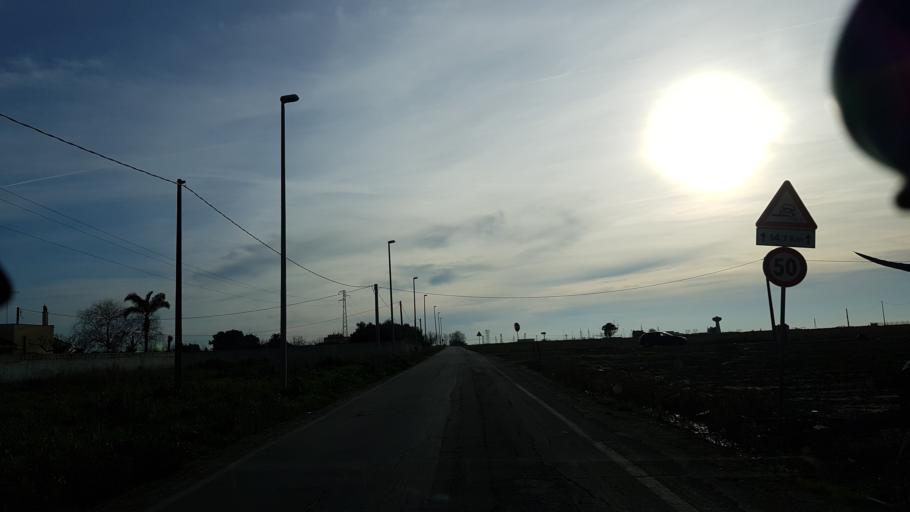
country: IT
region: Apulia
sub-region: Provincia di Brindisi
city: Brindisi
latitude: 40.6137
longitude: 17.9156
